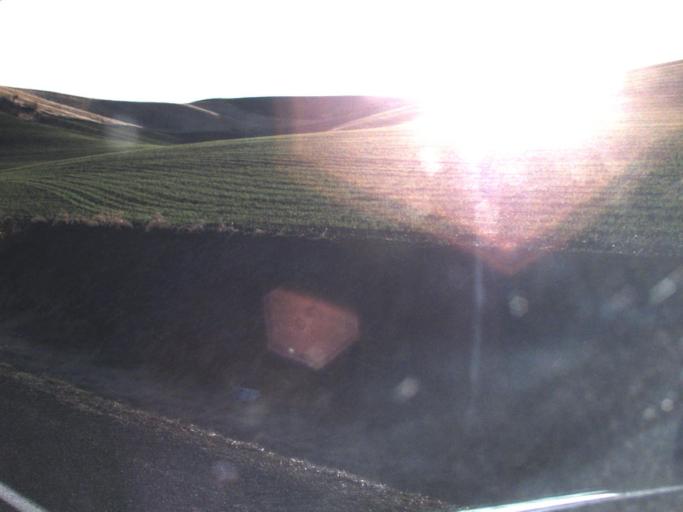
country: US
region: Washington
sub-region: Walla Walla County
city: Waitsburg
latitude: 46.1896
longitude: -118.1376
